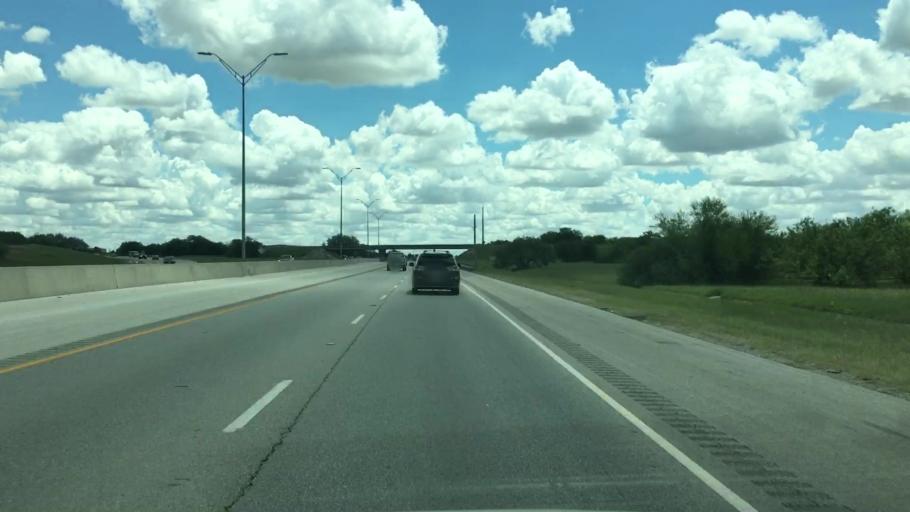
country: US
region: Texas
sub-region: Bexar County
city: Elmendorf
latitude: 29.3103
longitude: -98.4024
